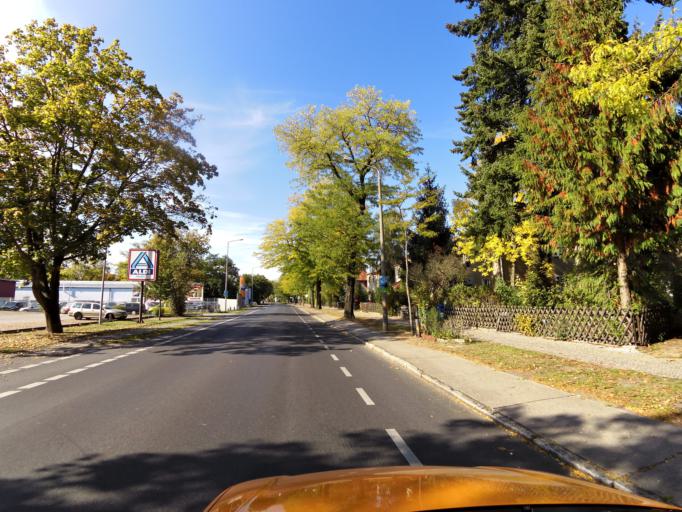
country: DE
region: Berlin
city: Wannsee
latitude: 52.3822
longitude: 13.1259
